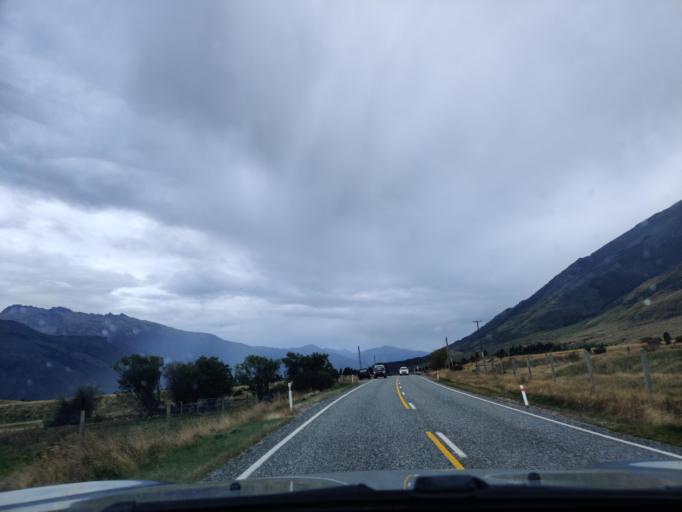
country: NZ
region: Otago
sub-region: Queenstown-Lakes District
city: Wanaka
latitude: -44.2955
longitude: 169.1965
